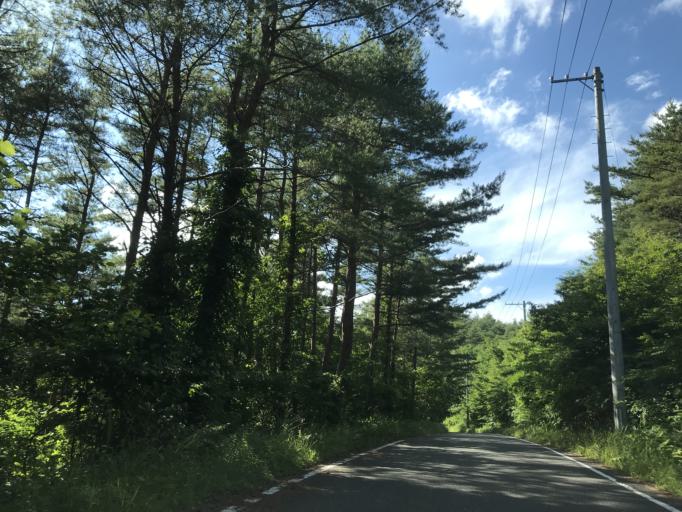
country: JP
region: Iwate
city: Ichinoseki
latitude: 38.8944
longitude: 140.8904
